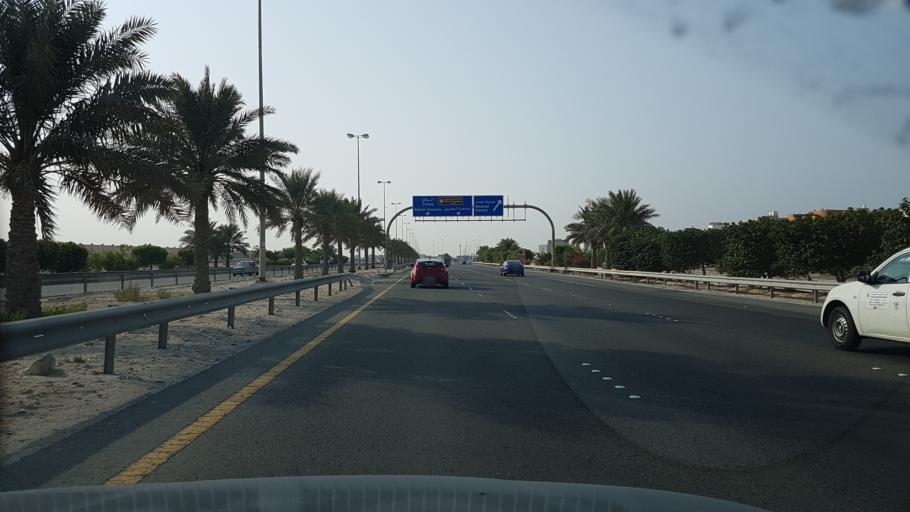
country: BH
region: Central Governorate
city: Madinat Hamad
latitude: 26.1076
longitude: 50.5111
